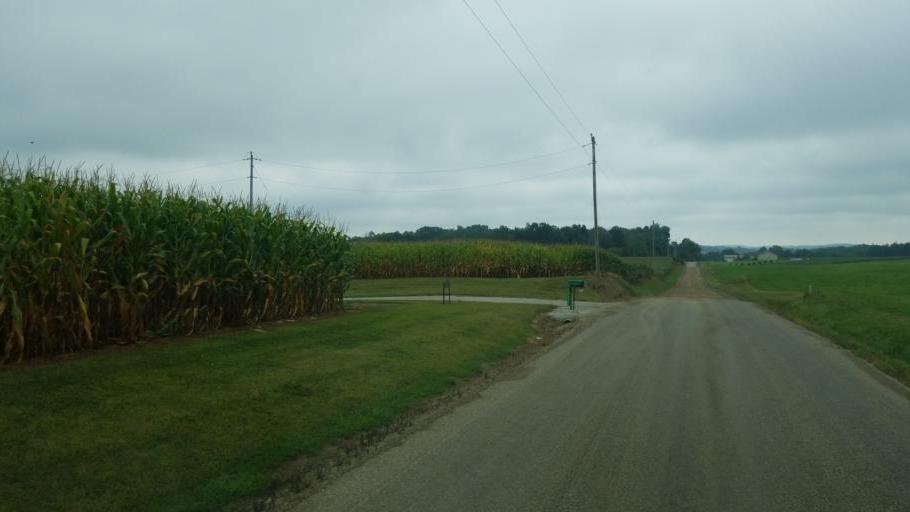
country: US
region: Ohio
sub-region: Licking County
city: Utica
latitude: 40.2523
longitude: -82.3992
